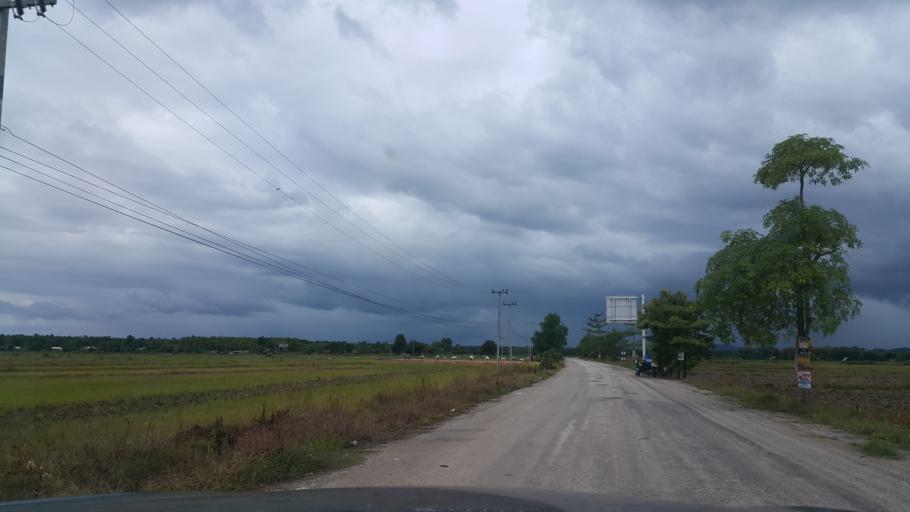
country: TH
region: Sukhothai
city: Thung Saliam
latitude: 17.3145
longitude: 99.5776
